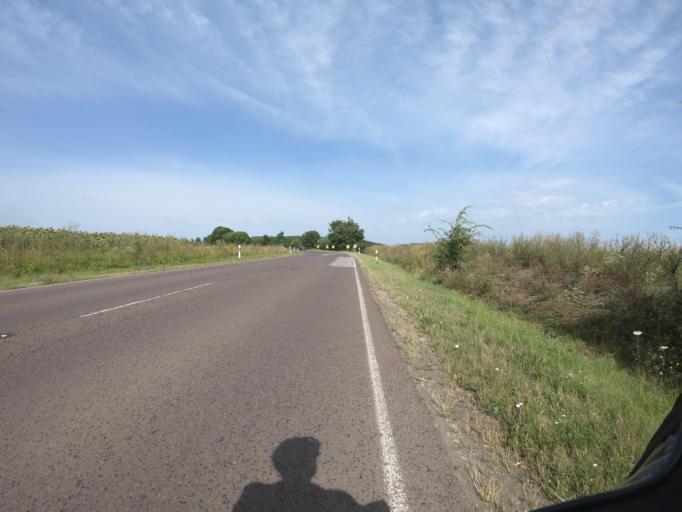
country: HU
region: Jasz-Nagykun-Szolnok
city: Tiszafured
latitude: 47.5973
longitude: 20.8236
